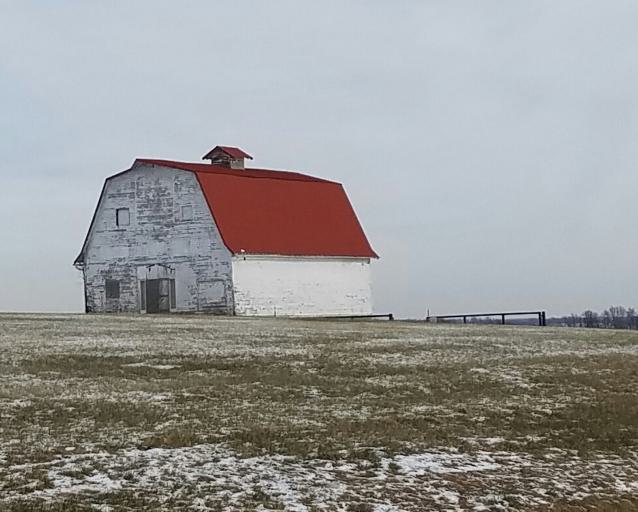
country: US
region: Missouri
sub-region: Lafayette County
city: Lexington
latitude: 39.1794
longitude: -93.7871
